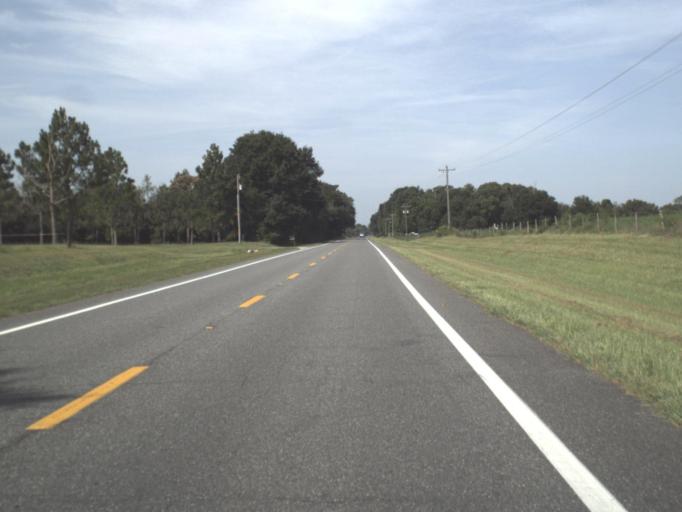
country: US
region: Florida
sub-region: Lafayette County
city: Mayo
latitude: 30.1975
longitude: -83.1105
